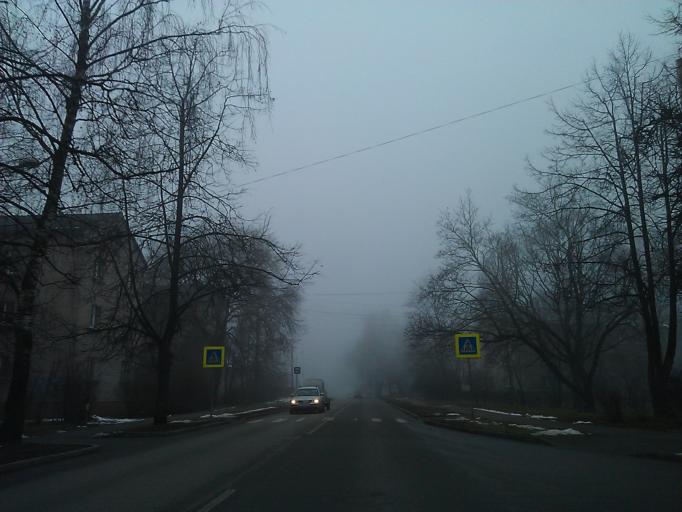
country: LV
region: Riga
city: Riga
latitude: 56.9140
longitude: 24.1110
